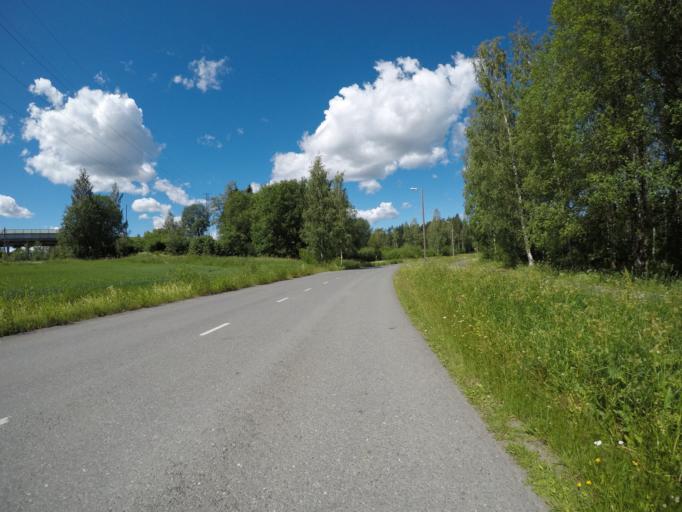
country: FI
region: Haeme
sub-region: Haemeenlinna
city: Haemeenlinna
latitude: 61.0207
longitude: 24.4272
